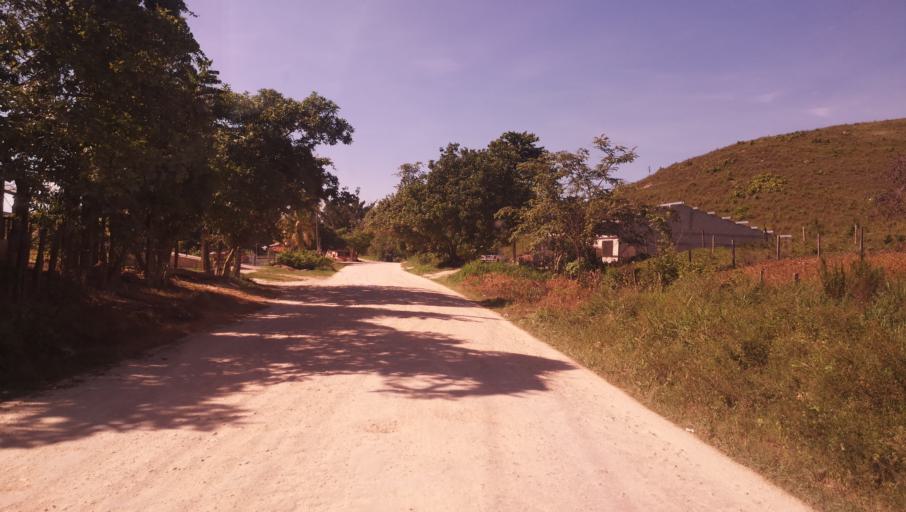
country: GT
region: Peten
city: Dolores
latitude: 16.7244
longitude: -89.3788
